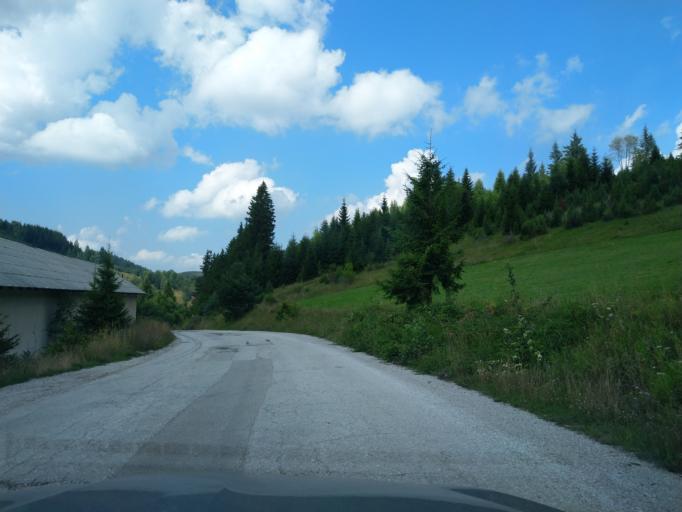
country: RS
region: Central Serbia
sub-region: Zlatiborski Okrug
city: Nova Varos
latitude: 43.5417
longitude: 19.9018
